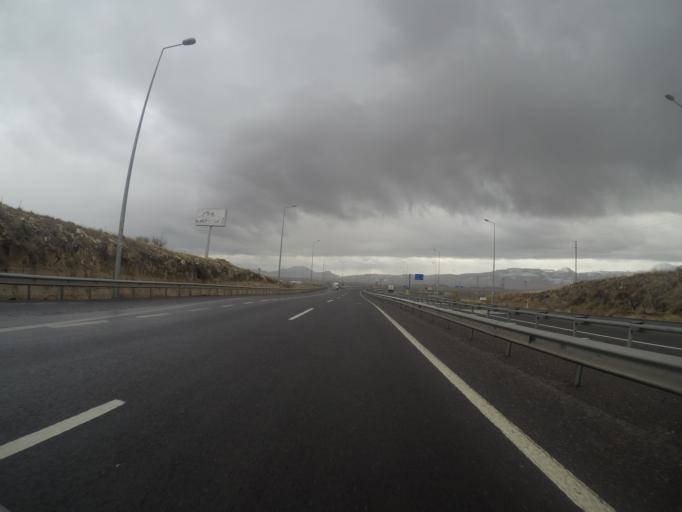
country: TR
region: Kayseri
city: Incesu
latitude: 38.6809
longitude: 35.2306
